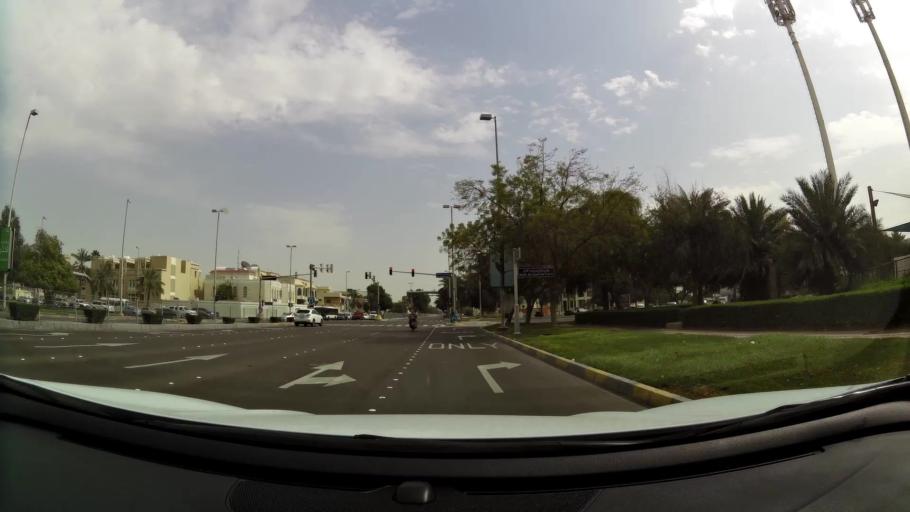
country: AE
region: Abu Dhabi
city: Abu Dhabi
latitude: 24.4661
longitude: 54.3653
